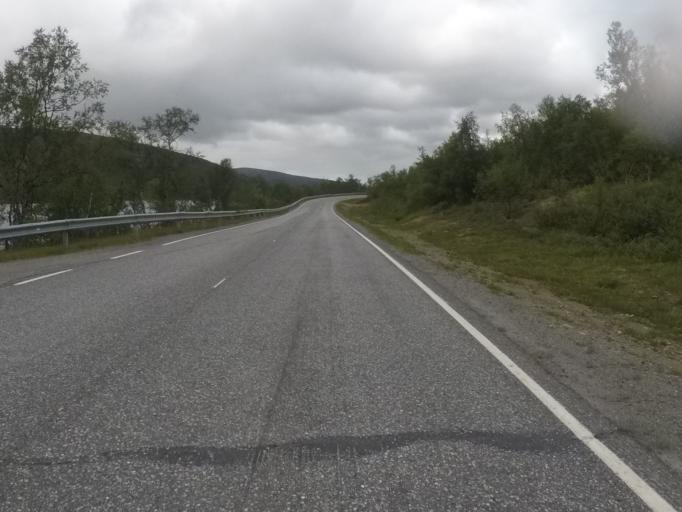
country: NO
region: Finnmark Fylke
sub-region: Alta
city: Alta
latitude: 69.6751
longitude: 23.4312
